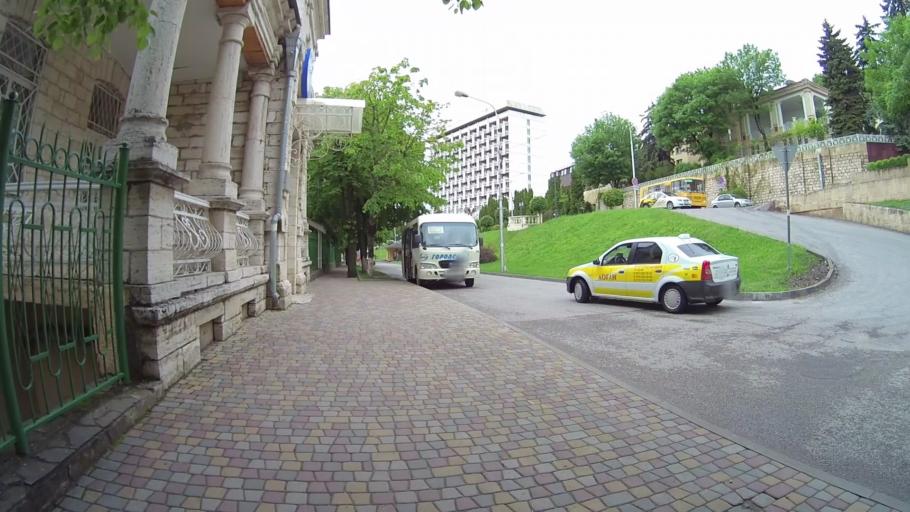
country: RU
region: Stavropol'skiy
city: Goryachevodskiy
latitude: 44.0450
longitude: 43.0982
